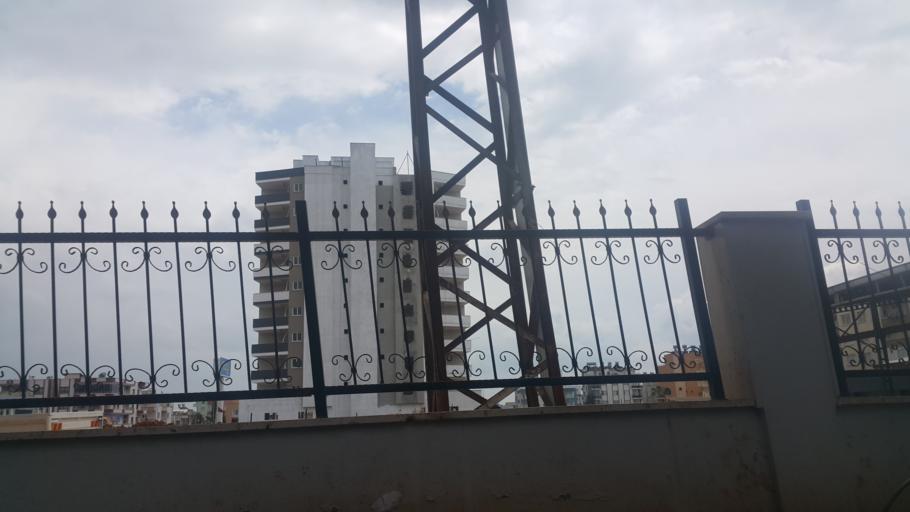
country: TR
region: Mersin
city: Mercin
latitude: 36.8181
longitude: 34.6061
